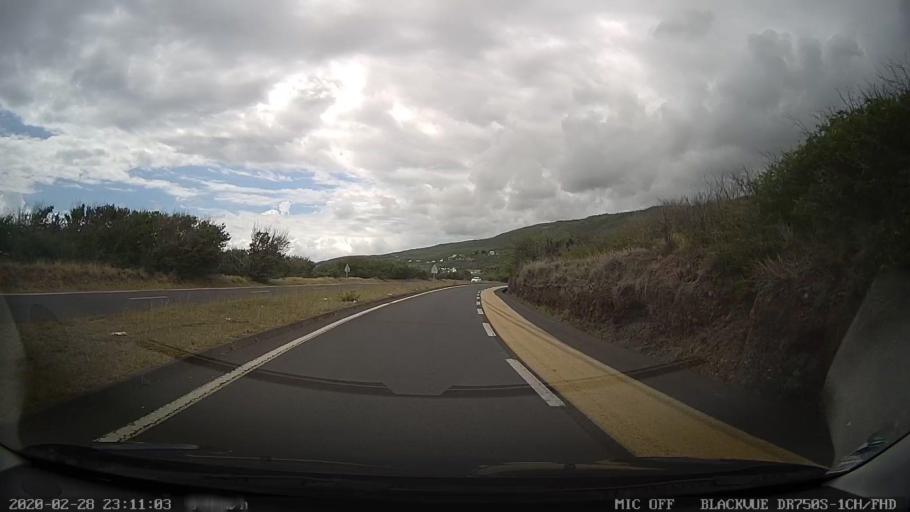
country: RE
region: Reunion
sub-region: Reunion
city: Trois-Bassins
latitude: -21.1137
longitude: 55.2559
